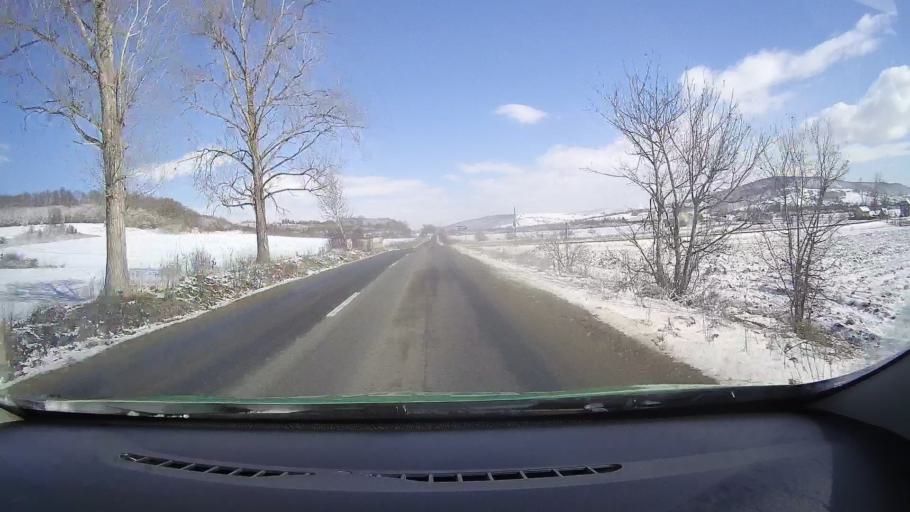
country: RO
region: Sibiu
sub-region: Comuna Nocrich
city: Nocrich
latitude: 45.8415
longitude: 24.4192
